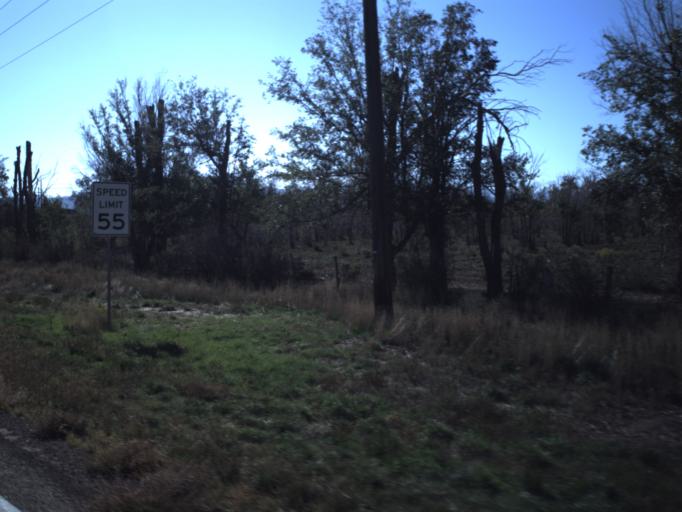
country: US
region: Utah
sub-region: Washington County
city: Enterprise
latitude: 37.7100
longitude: -113.6578
